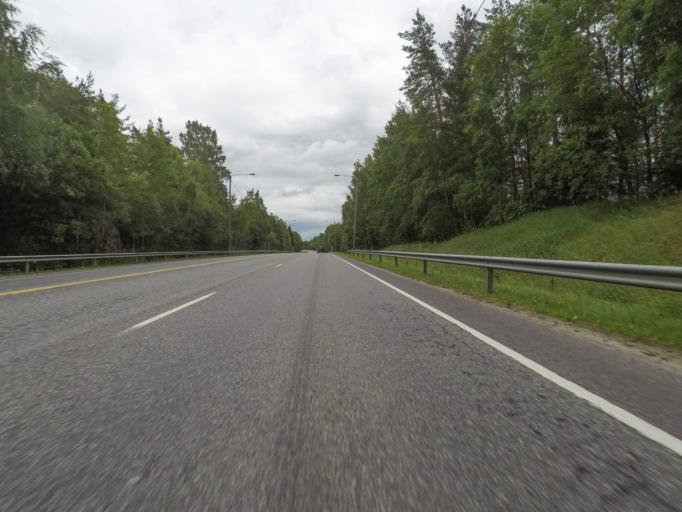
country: FI
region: Varsinais-Suomi
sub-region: Turku
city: Kaarina
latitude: 60.4671
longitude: 22.3832
